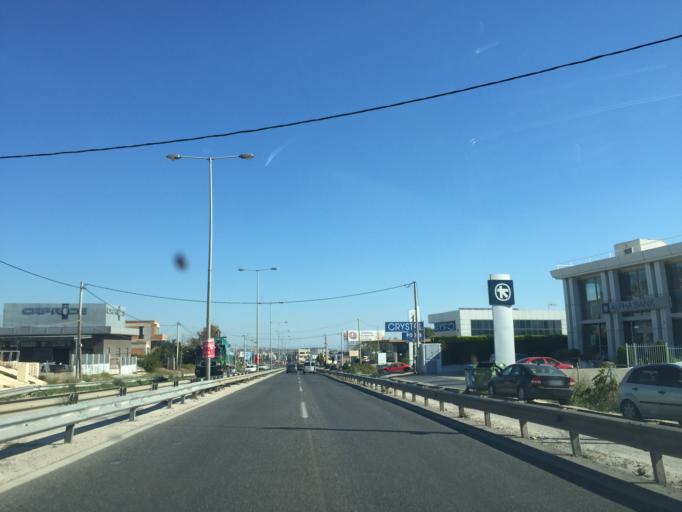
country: GR
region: Attica
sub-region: Nomarchia Anatolikis Attikis
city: Koropi
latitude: 37.8736
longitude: 23.8617
